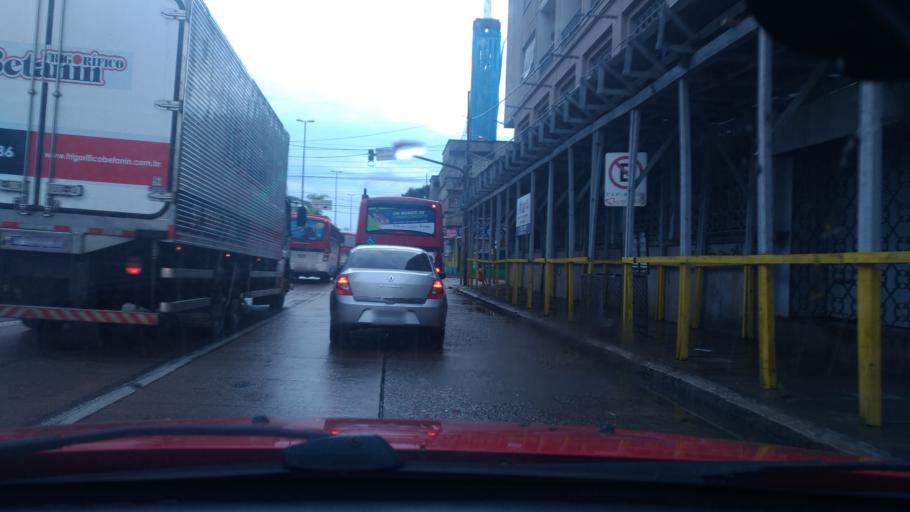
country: BR
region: Rio Grande do Sul
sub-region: Porto Alegre
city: Porto Alegre
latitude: -30.0108
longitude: -51.2027
